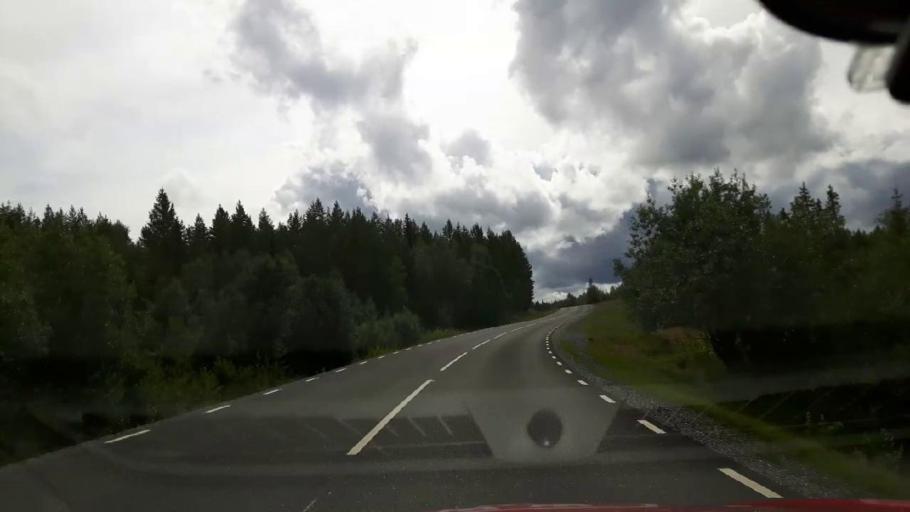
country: NO
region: Nord-Trondelag
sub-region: Lierne
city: Sandvika
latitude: 64.6045
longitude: 14.1203
